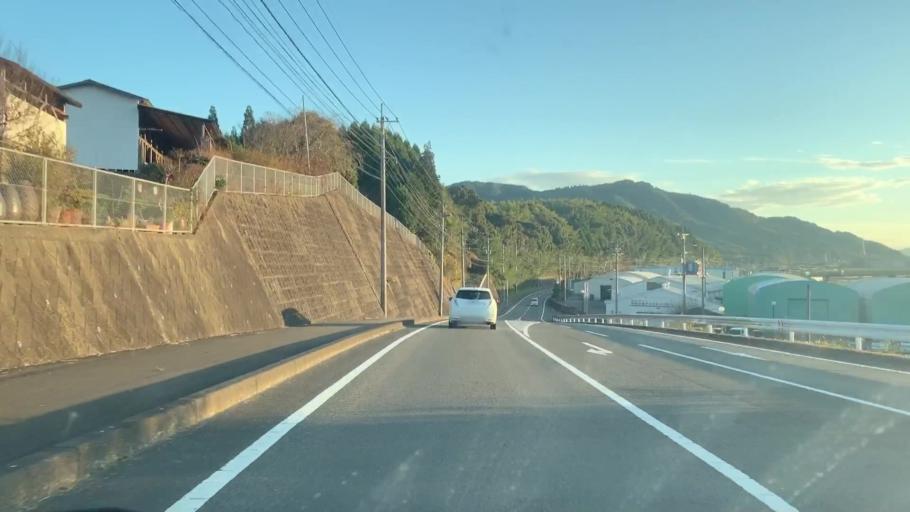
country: JP
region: Saga Prefecture
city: Imaricho-ko
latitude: 33.2910
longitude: 129.9705
